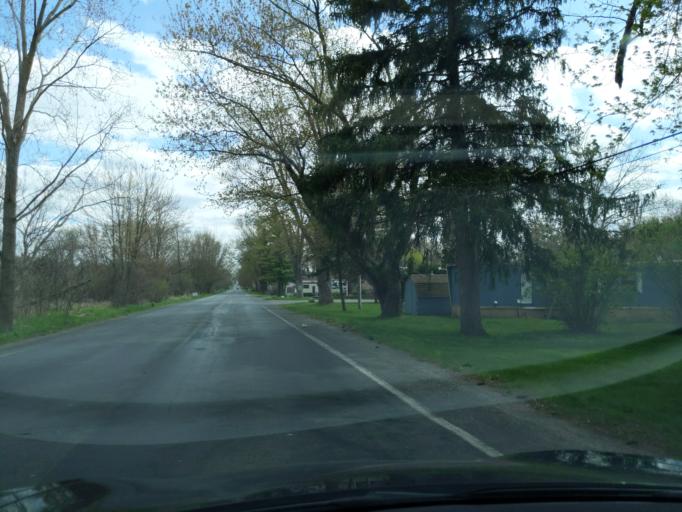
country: US
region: Michigan
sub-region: Ingham County
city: Holt
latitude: 42.6246
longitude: -84.5429
